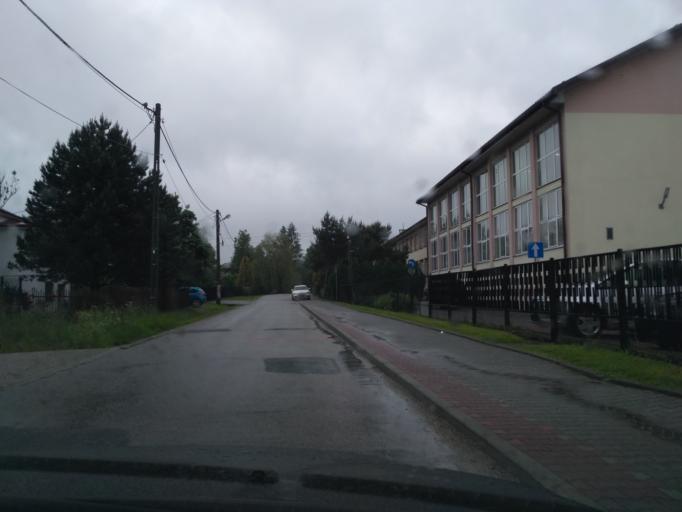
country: PL
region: Lesser Poland Voivodeship
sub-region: Powiat gorlicki
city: Gorlice
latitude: 49.6663
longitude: 21.1428
